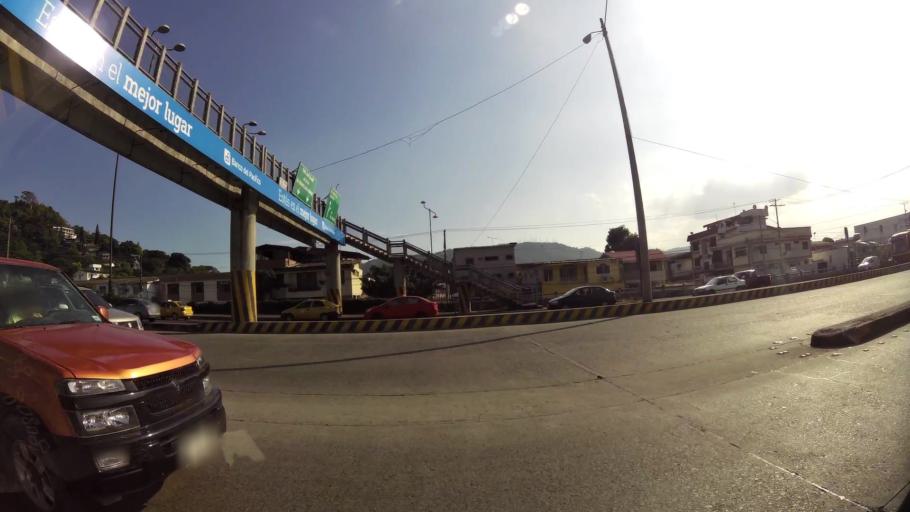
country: EC
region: Guayas
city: Guayaquil
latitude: -2.1601
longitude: -79.9281
